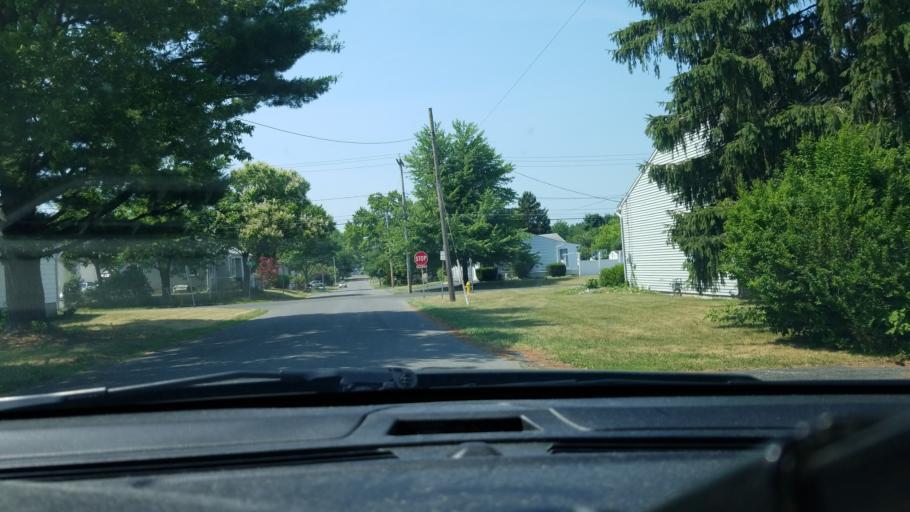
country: US
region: New York
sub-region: Onondaga County
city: Galeville
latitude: 43.0941
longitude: -76.1778
